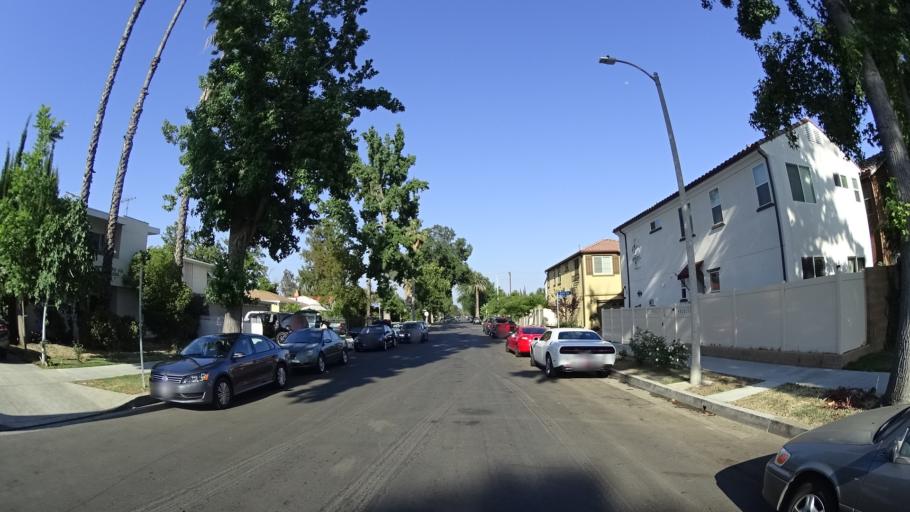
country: US
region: California
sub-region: Los Angeles County
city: Van Nuys
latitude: 34.1778
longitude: -118.4477
